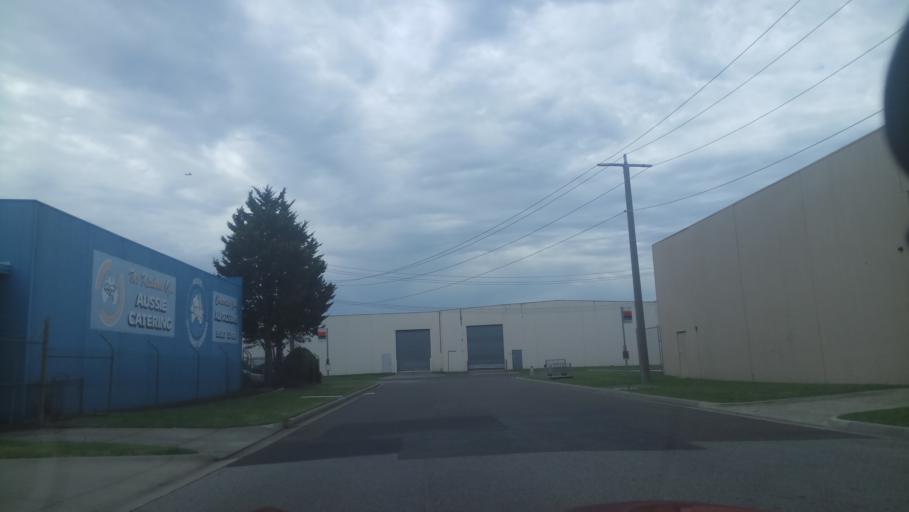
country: AU
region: Victoria
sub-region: Kingston
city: Aspendale Gardens
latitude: -38.0047
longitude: 145.1097
